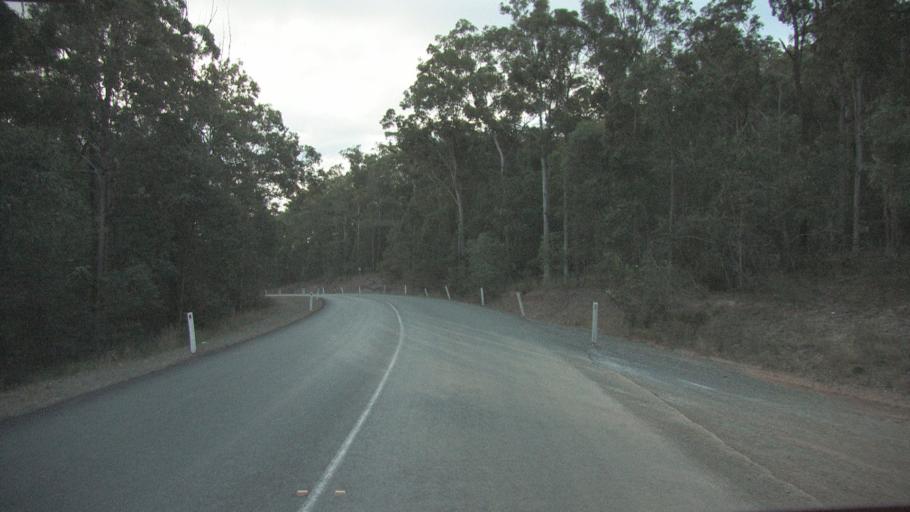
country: AU
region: Queensland
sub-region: Logan
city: Chambers Flat
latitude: -27.8009
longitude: 153.1443
